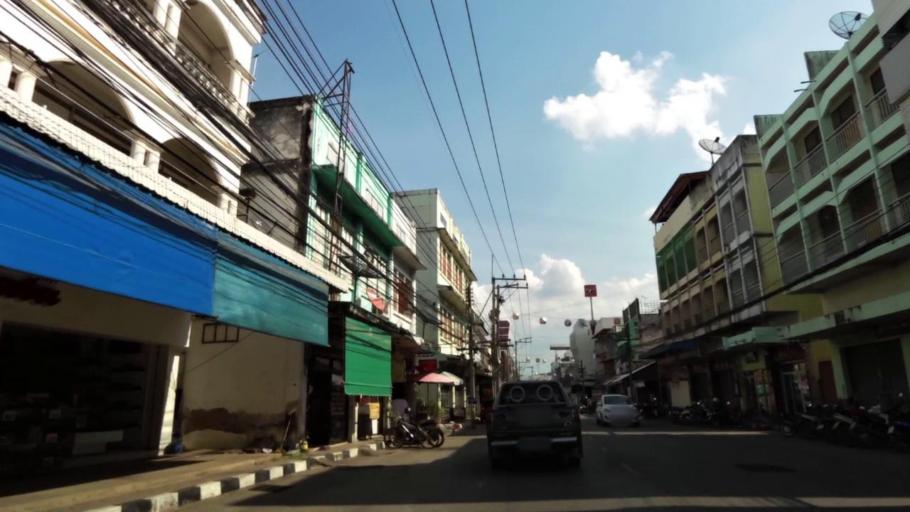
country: TH
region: Phrae
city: Phrae
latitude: 18.1397
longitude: 100.1456
